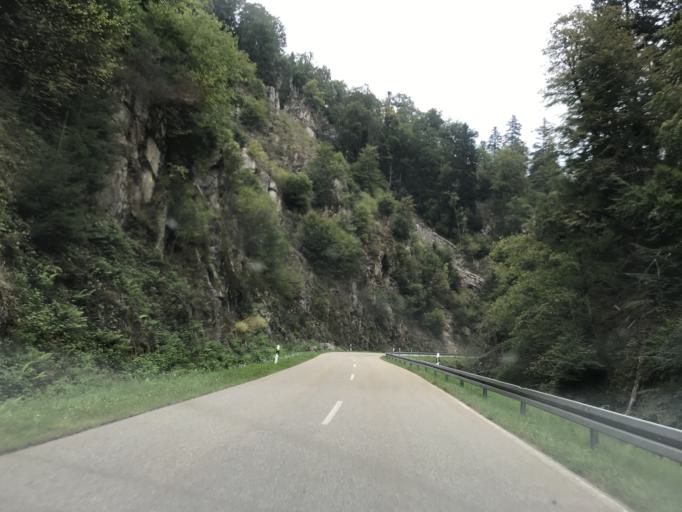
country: DE
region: Baden-Wuerttemberg
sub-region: Freiburg Region
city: Herrischried
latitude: 47.6786
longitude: 7.9463
